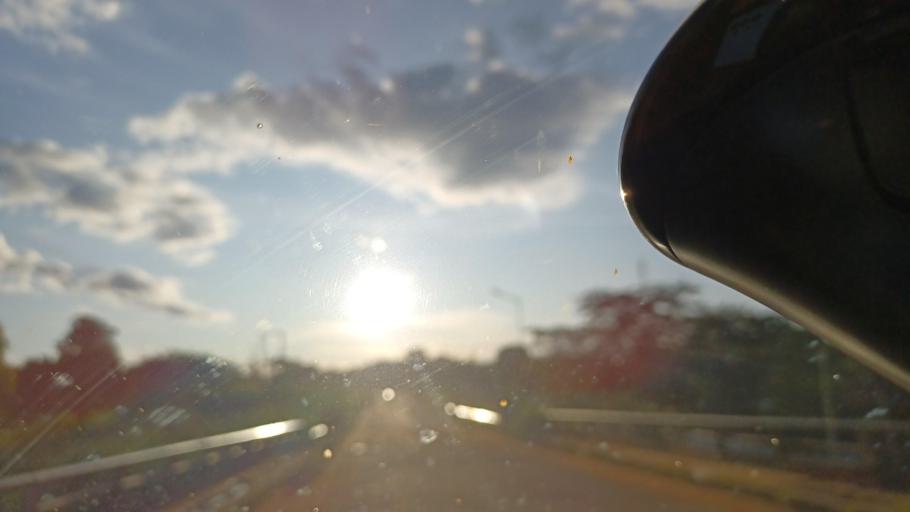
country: ZM
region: North-Western
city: Kasempa
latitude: -13.4582
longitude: 25.8451
